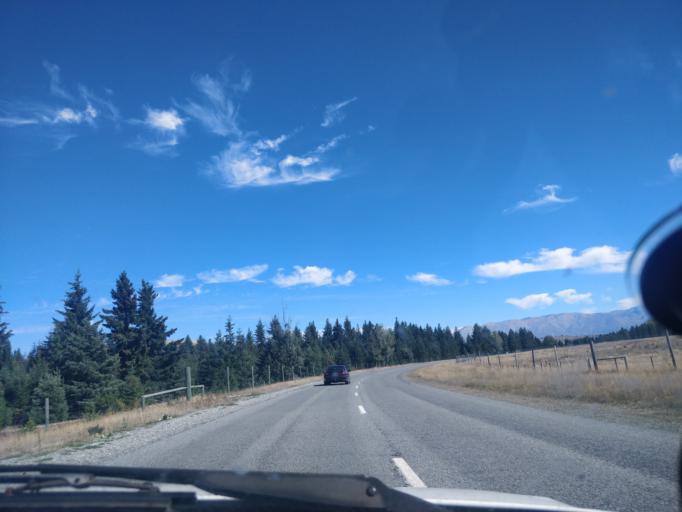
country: NZ
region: Otago
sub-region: Queenstown-Lakes District
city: Wanaka
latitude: -44.2717
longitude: 170.0606
